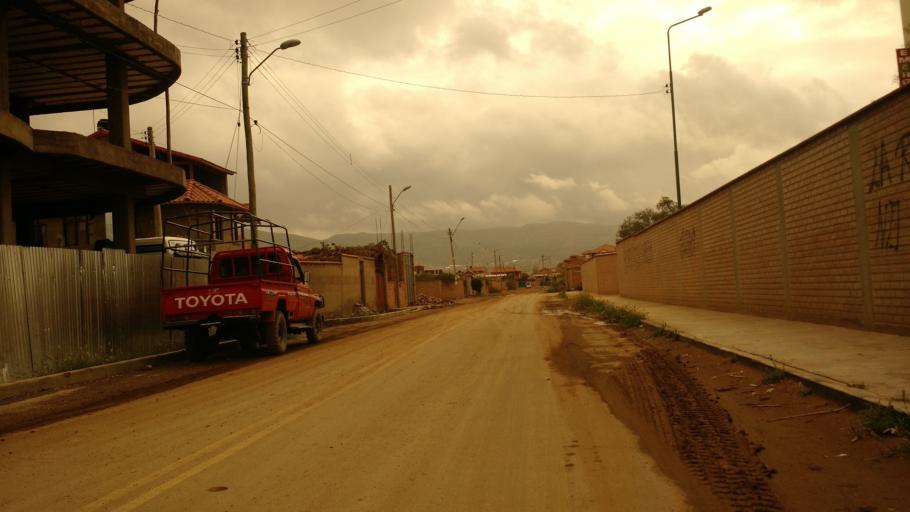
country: BO
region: Cochabamba
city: Cochabamba
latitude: -17.4501
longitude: -66.1506
